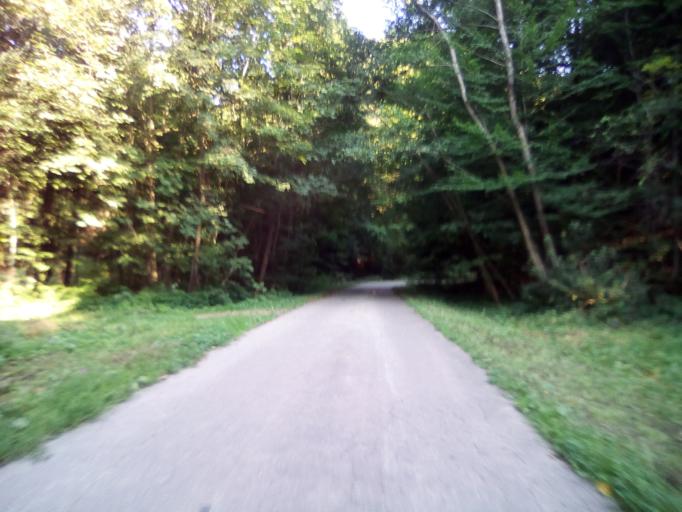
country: PL
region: Subcarpathian Voivodeship
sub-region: Powiat brzozowski
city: Domaradz
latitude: 49.8118
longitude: 21.9646
